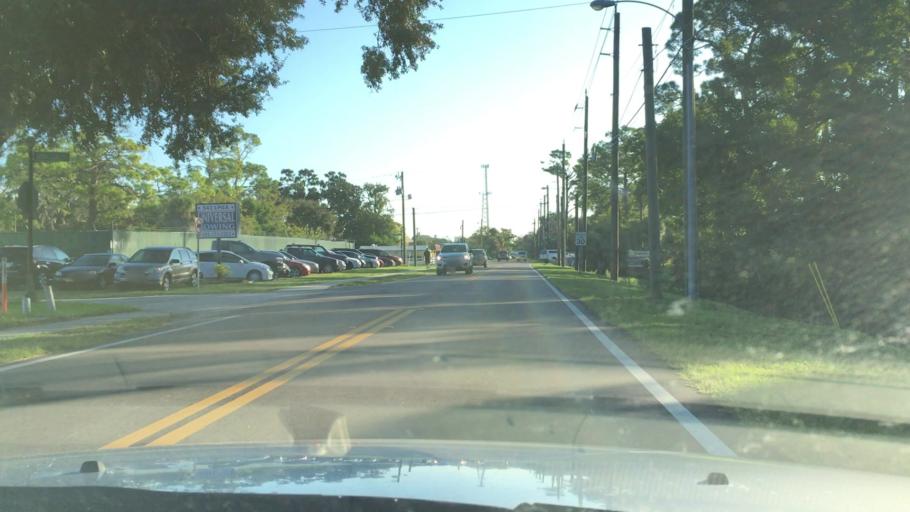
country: US
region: Florida
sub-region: Volusia County
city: Holly Hill
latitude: 29.2428
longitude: -81.0489
